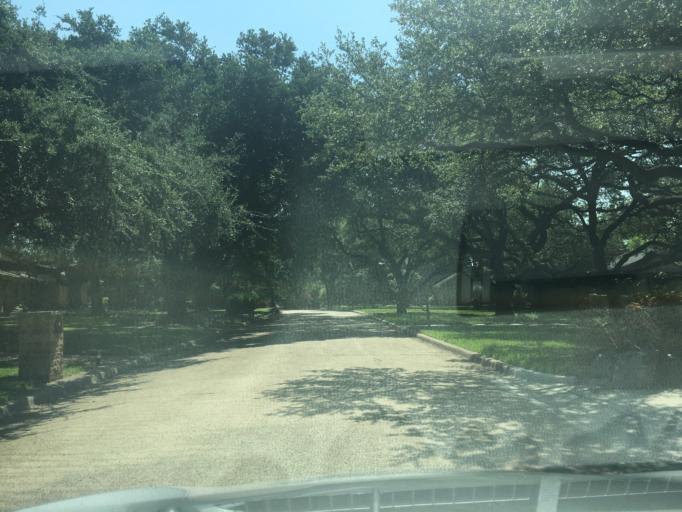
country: US
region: Texas
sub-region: Dallas County
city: University Park
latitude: 32.9114
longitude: -96.7917
